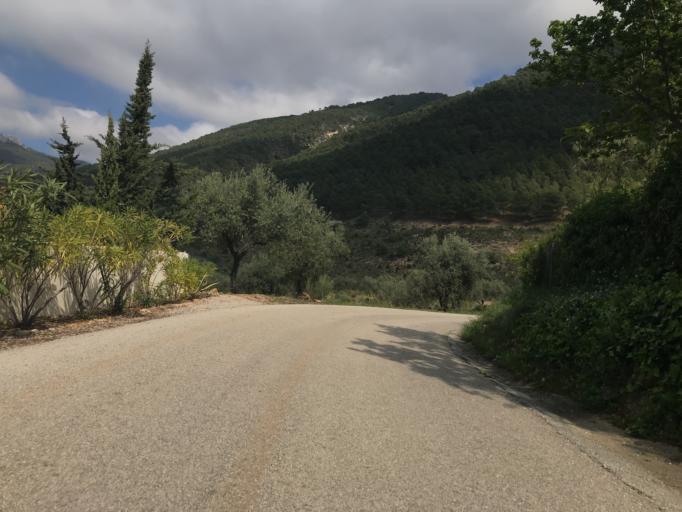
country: ES
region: Andalusia
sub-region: Provincia de Malaga
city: Alcaucin
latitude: 36.9115
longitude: -4.1086
